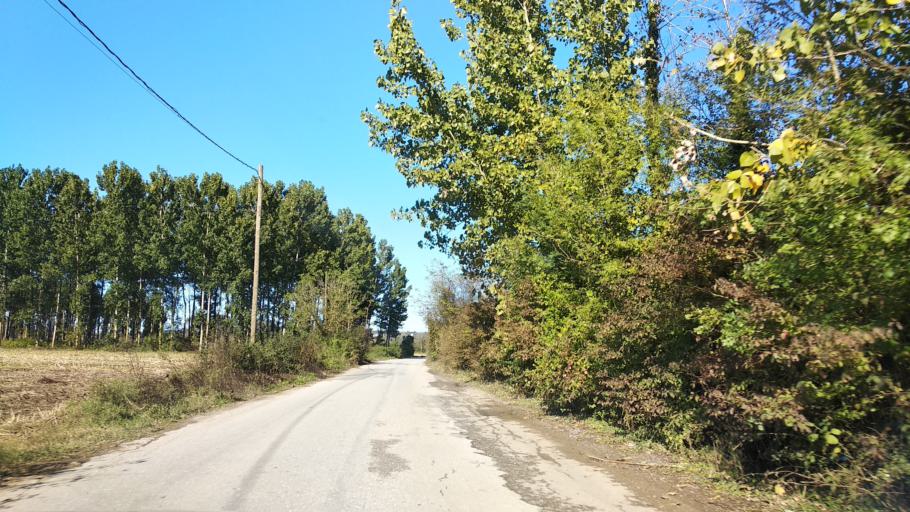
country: TR
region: Sakarya
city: Ortakoy
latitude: 41.0302
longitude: 30.6073
